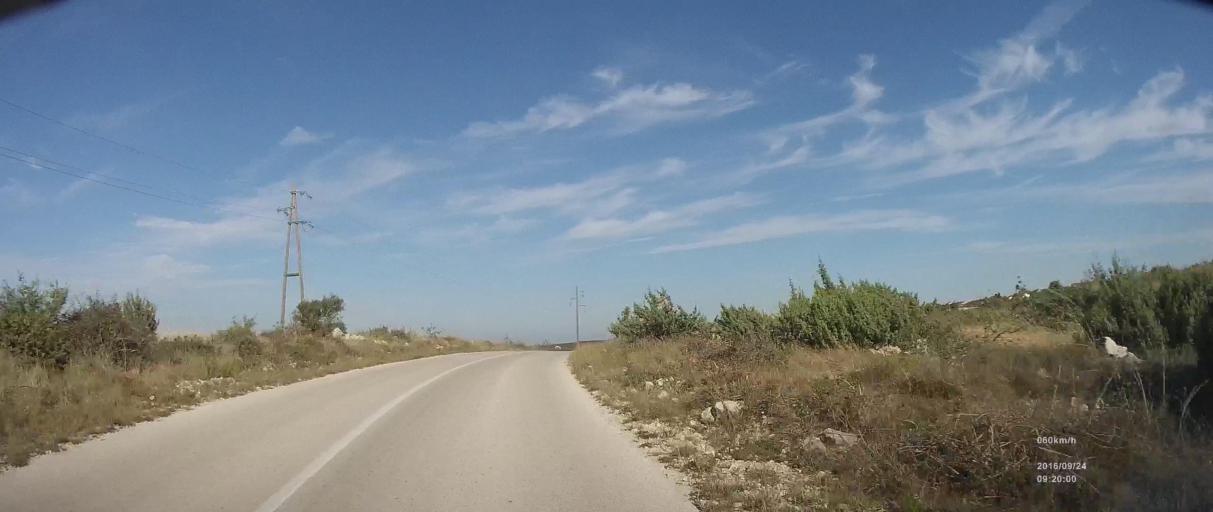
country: HR
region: Zadarska
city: Polaca
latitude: 44.0657
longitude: 15.4995
